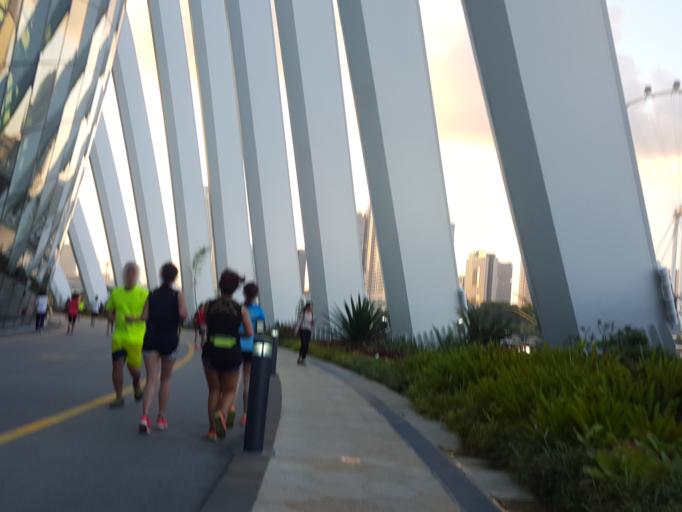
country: SG
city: Singapore
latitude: 1.2847
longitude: 103.8654
